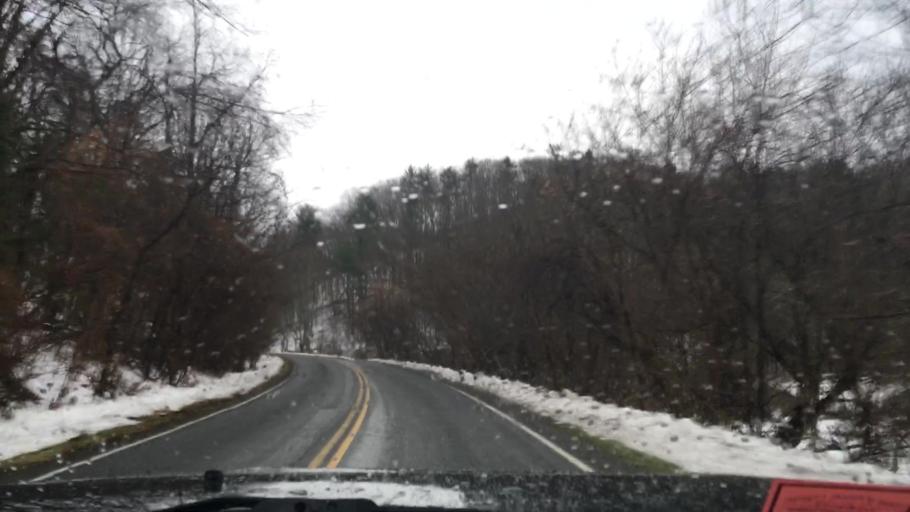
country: US
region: Virginia
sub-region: Pulaski County
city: Pulaski
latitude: 37.0137
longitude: -80.7032
